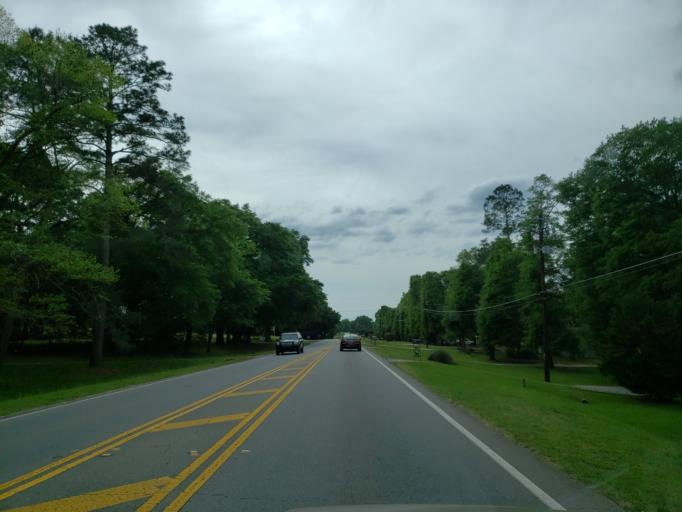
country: US
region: Georgia
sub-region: Houston County
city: Perry
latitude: 32.4469
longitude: -83.7596
